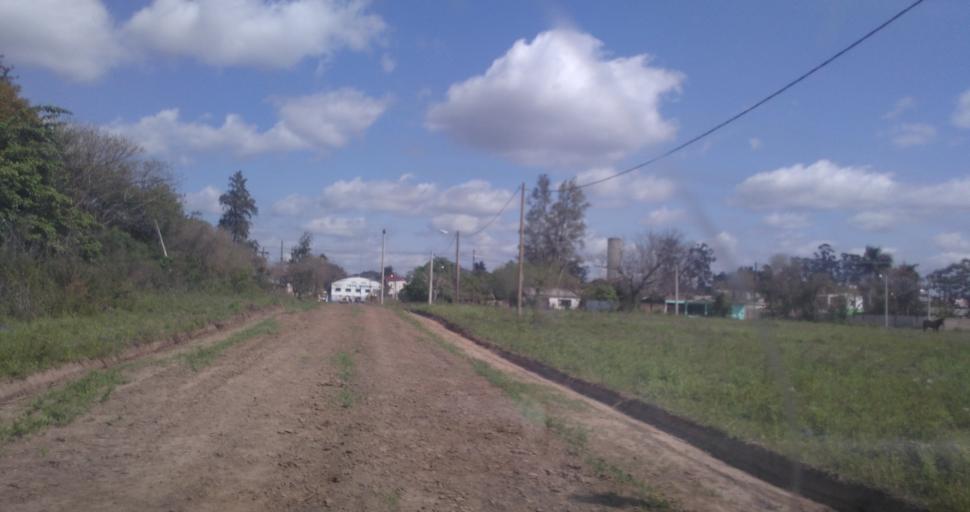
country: AR
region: Chaco
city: Fontana
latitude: -27.4279
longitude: -59.0233
